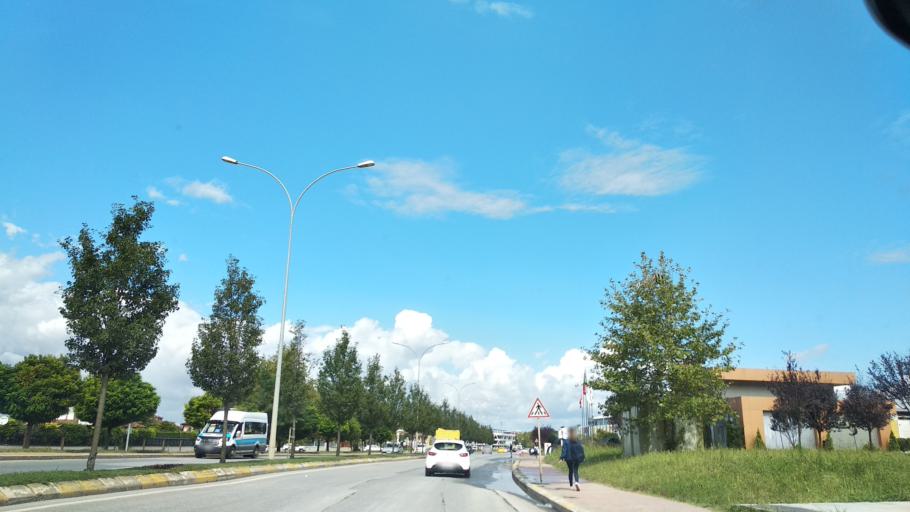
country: TR
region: Sakarya
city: Adapazari
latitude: 40.7760
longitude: 30.3639
